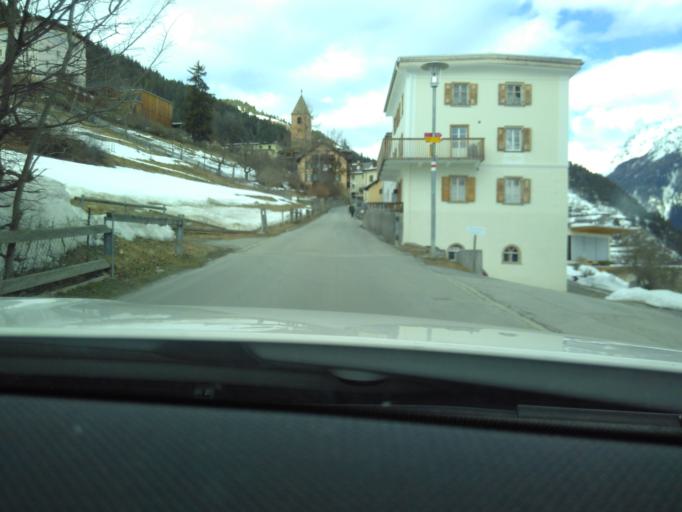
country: CH
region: Grisons
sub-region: Inn District
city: Scuol
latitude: 46.8328
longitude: 10.3802
